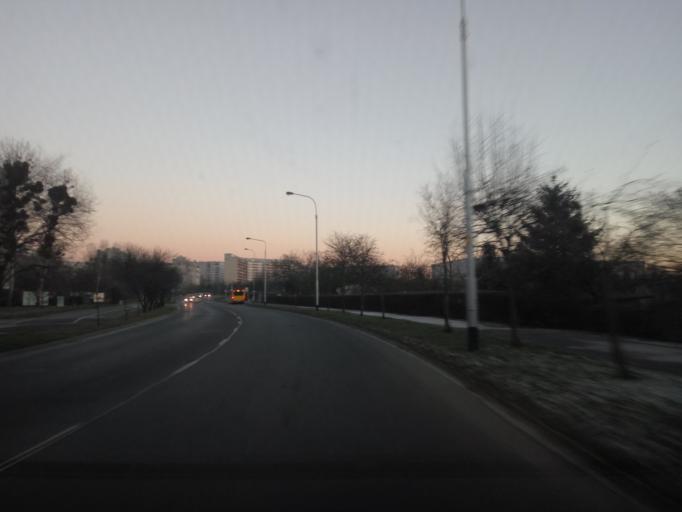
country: PL
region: Lower Silesian Voivodeship
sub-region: Powiat wroclawski
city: Bielany Wroclawskie
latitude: 51.1118
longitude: 16.9508
